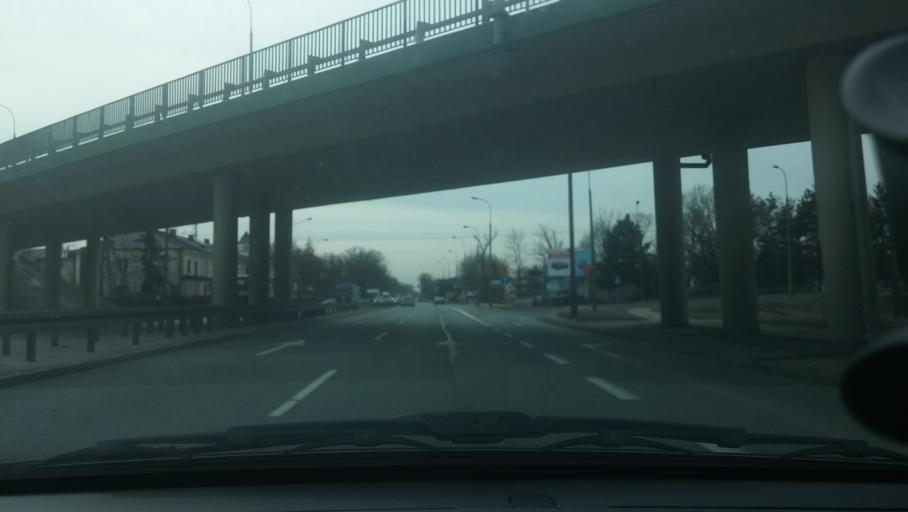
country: PL
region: Masovian Voivodeship
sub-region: Powiat wolominski
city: Slupno
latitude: 52.3640
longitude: 21.1386
